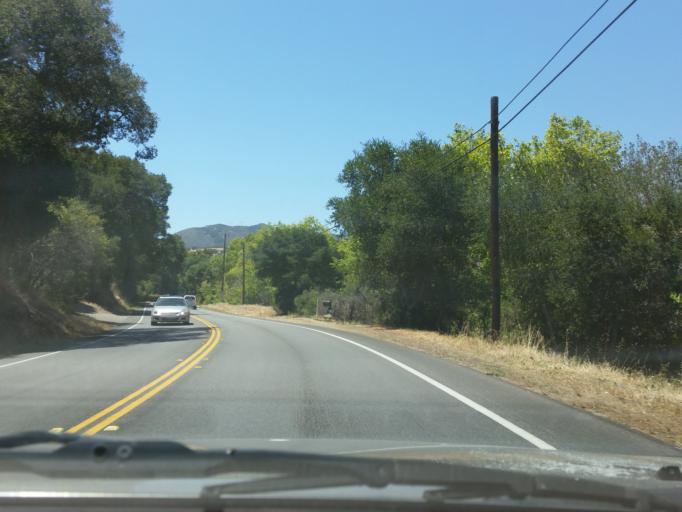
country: US
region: California
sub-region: San Luis Obispo County
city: Avila Beach
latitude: 35.1845
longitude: -120.7091
